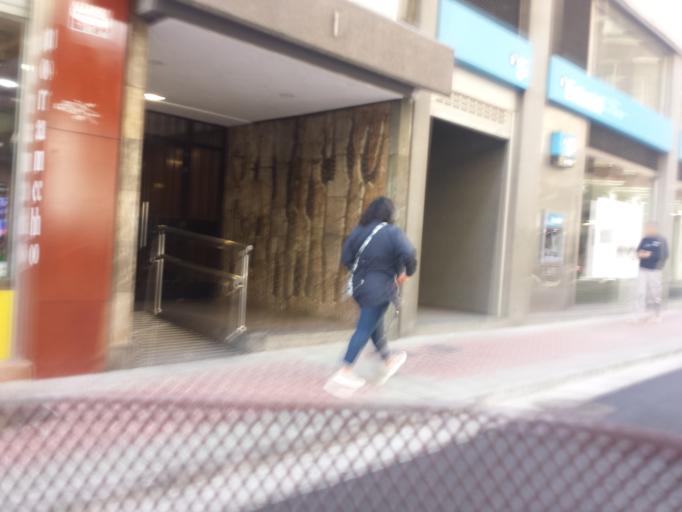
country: ES
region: Aragon
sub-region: Provincia de Zaragoza
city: Zaragoza
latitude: 41.6507
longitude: -0.8805
